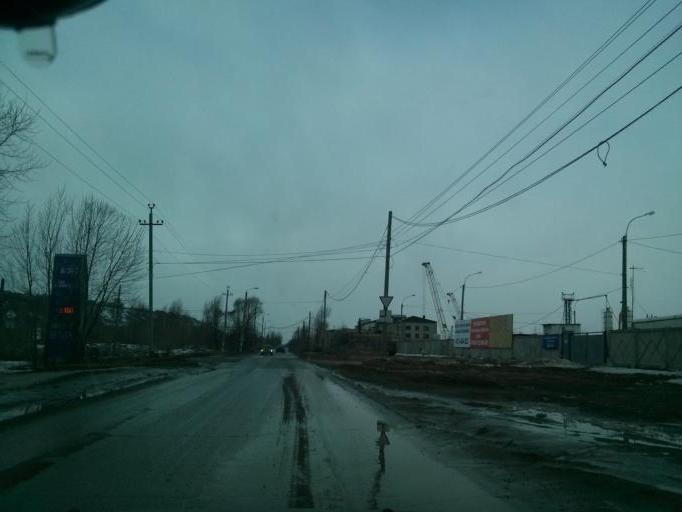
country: RU
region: Nizjnij Novgorod
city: Afonino
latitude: 56.2935
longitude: 44.1107
